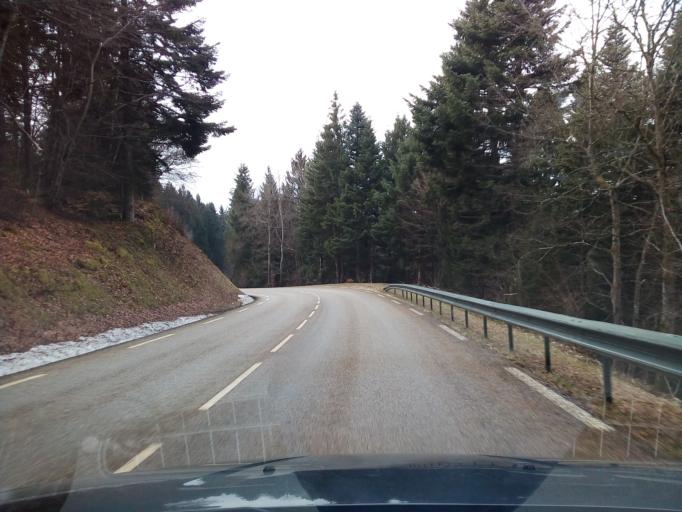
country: FR
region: Rhone-Alpes
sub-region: Departement de l'Isere
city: Revel
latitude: 45.1543
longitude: 5.8685
